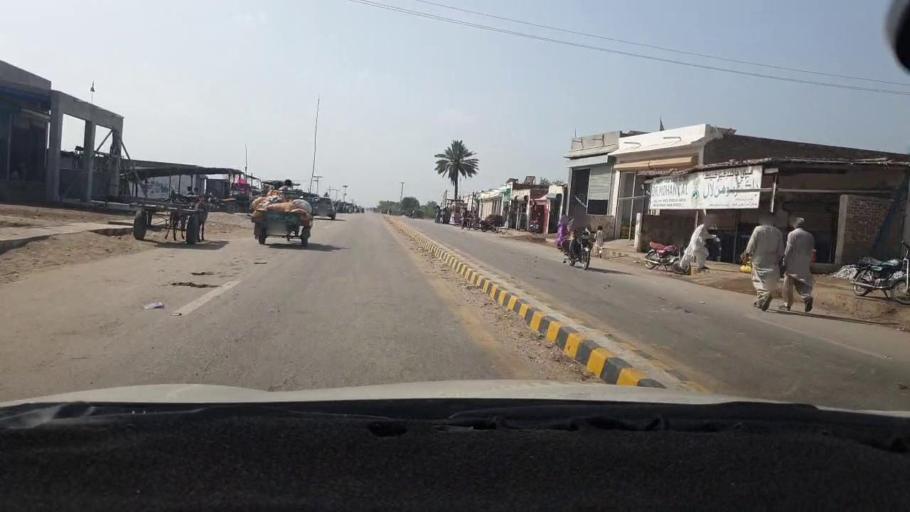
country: PK
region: Sindh
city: Tando Mittha Khan
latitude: 25.7939
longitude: 69.0716
